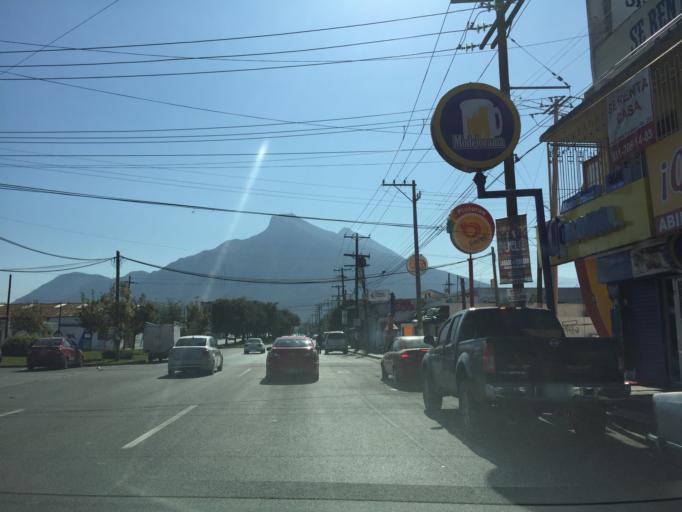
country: MX
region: Nuevo Leon
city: Guadalupe
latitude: 25.6887
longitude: -100.2300
